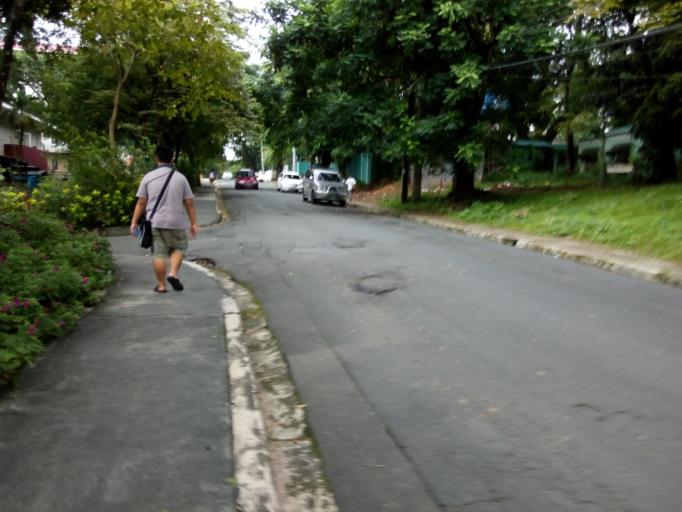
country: PH
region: Metro Manila
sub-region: Quezon City
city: Quezon City
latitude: 14.6578
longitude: 121.0706
